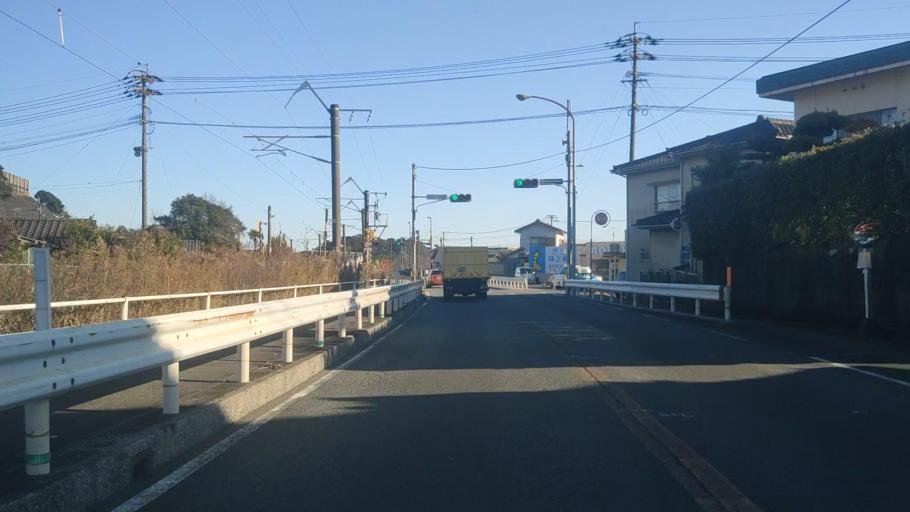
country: JP
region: Miyazaki
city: Nobeoka
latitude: 32.5117
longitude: 131.6809
